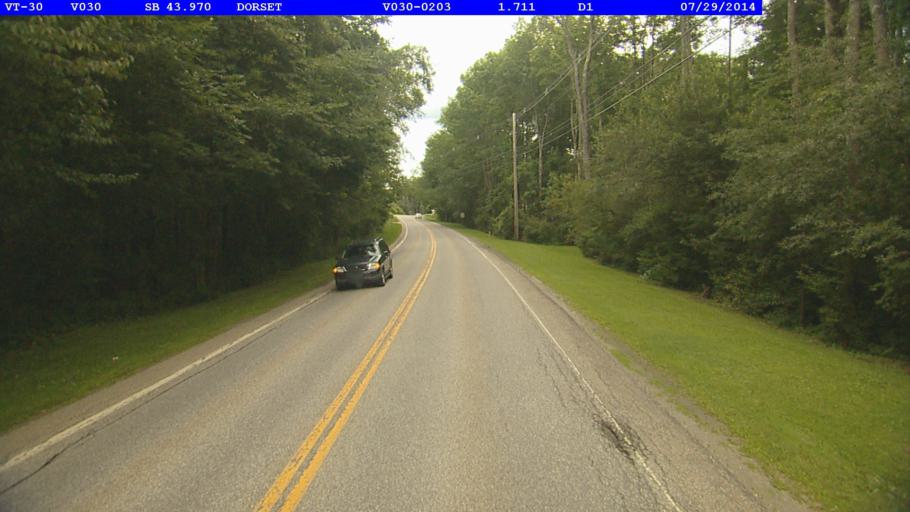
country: US
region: Vermont
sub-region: Bennington County
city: Manchester Center
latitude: 43.2343
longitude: -73.0824
